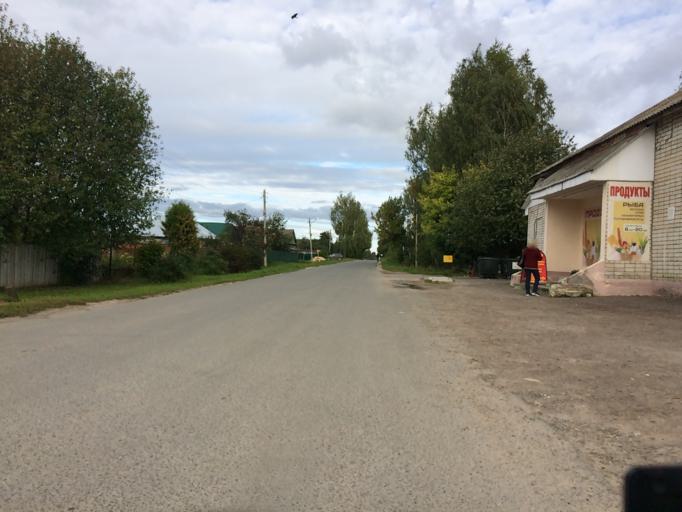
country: RU
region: Mariy-El
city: Yoshkar-Ola
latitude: 56.6571
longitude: 47.9742
